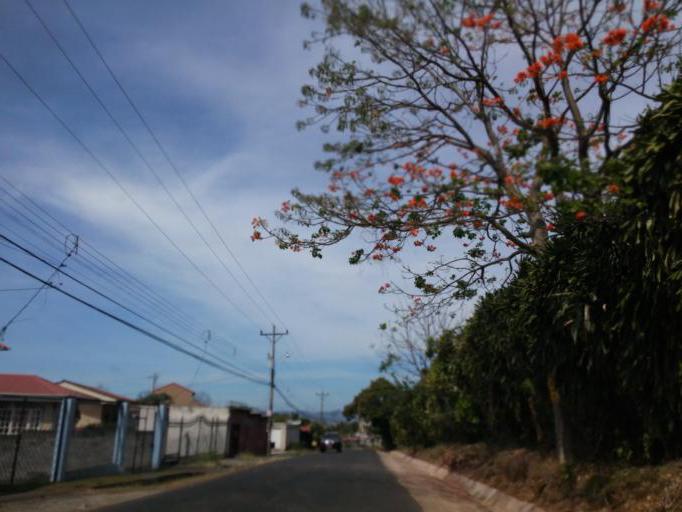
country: CR
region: Alajuela
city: Sabanilla
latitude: 10.0443
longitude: -84.2294
